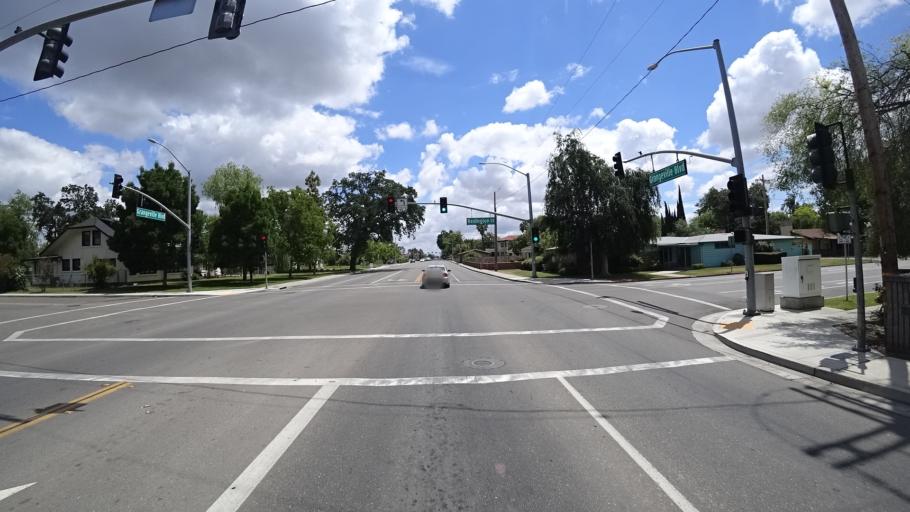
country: US
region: California
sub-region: Kings County
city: Hanford
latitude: 36.3426
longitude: -119.6496
